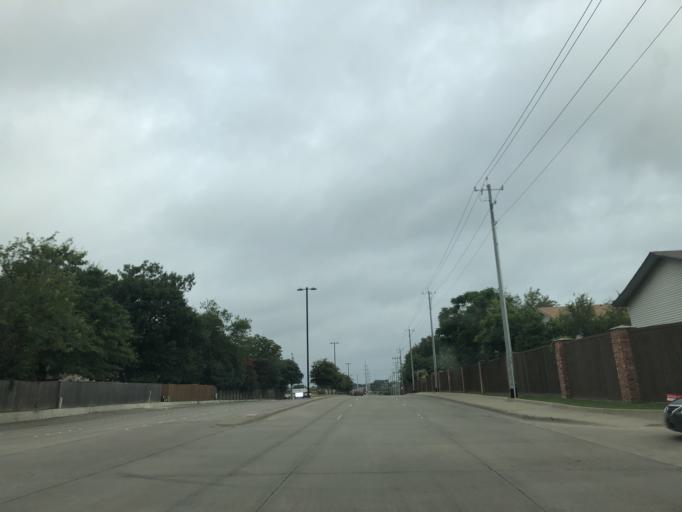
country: US
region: Texas
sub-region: Dallas County
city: Garland
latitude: 32.8590
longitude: -96.6398
